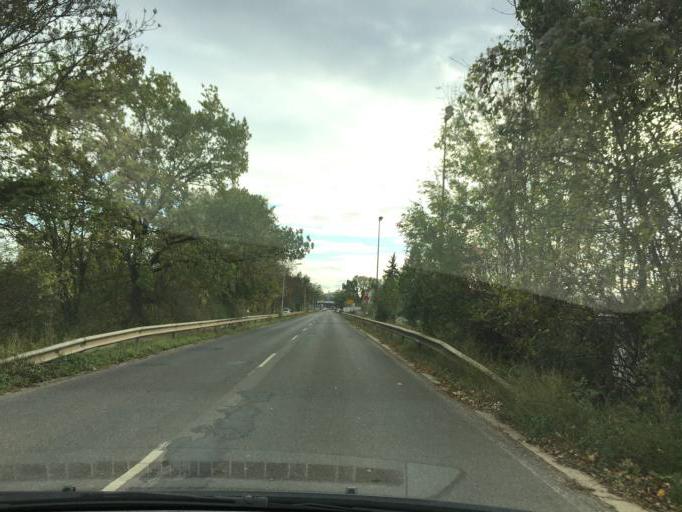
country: DE
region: North Rhine-Westphalia
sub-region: Regierungsbezirk Koln
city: Dueren
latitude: 50.8032
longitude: 6.4628
